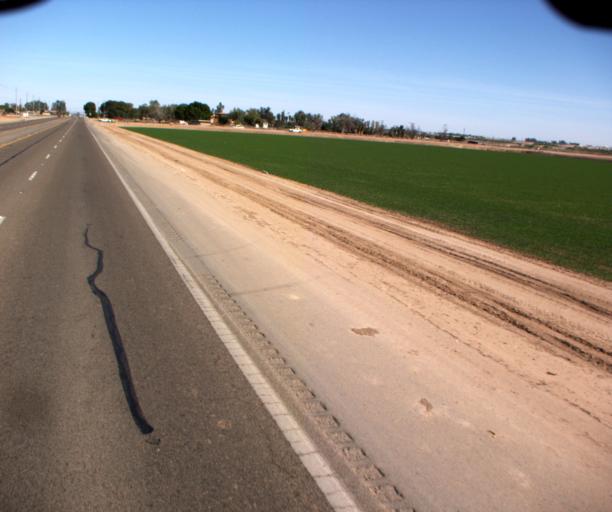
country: US
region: Arizona
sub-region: Yuma County
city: Somerton
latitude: 32.6308
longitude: -114.6498
